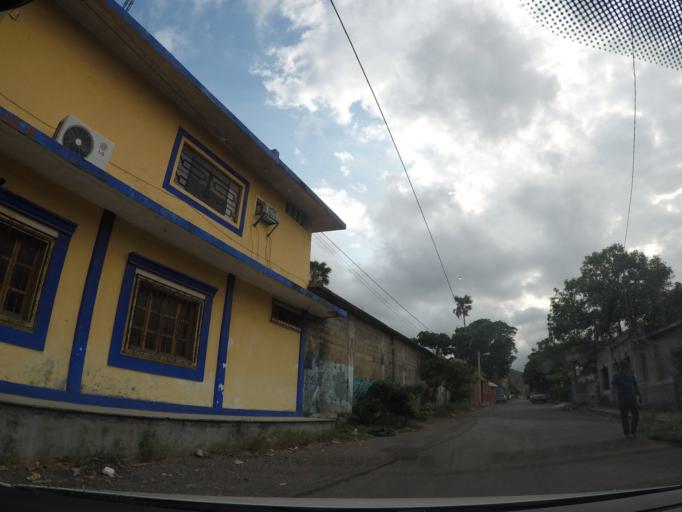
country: MX
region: Oaxaca
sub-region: Salina Cruz
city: Salina Cruz
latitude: 16.2068
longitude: -95.2060
